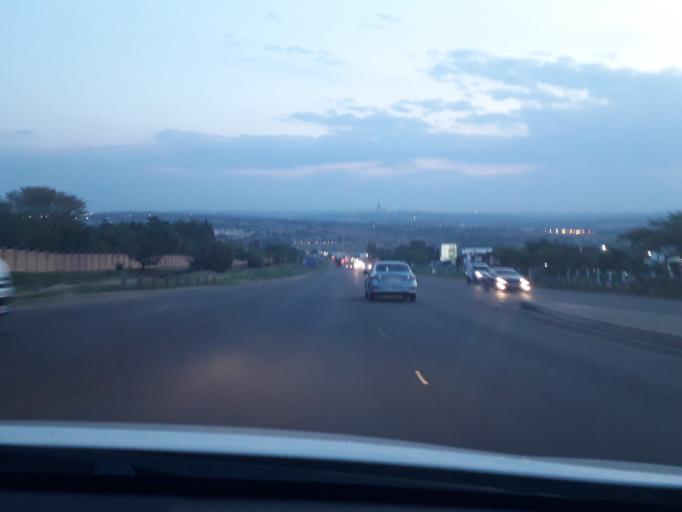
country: ZA
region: Gauteng
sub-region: City of Johannesburg Metropolitan Municipality
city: Midrand
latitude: -25.9910
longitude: 28.0768
